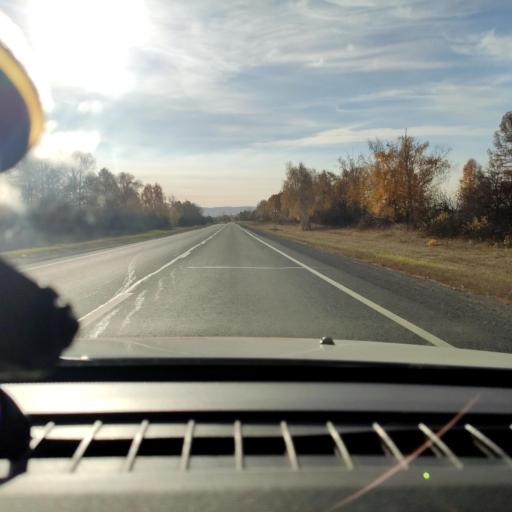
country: RU
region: Samara
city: Volzhskiy
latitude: 53.4704
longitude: 50.1234
